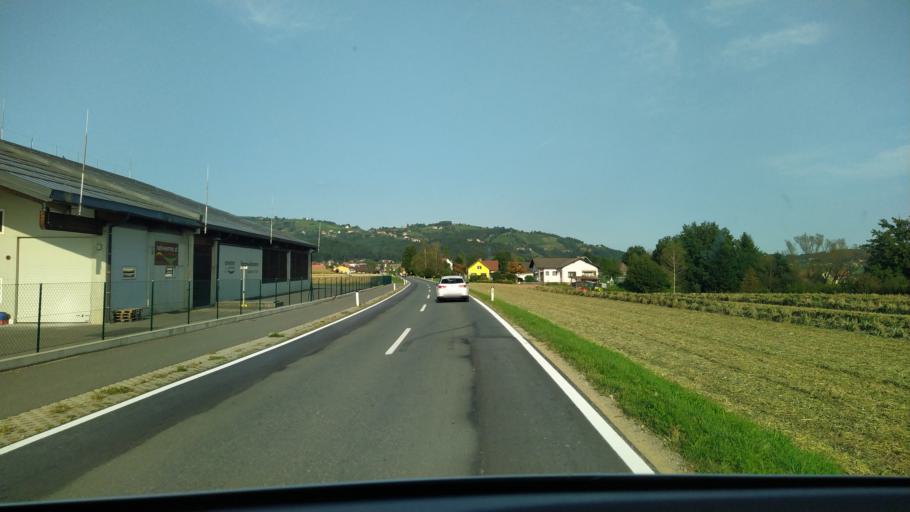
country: AT
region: Styria
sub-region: Politischer Bezirk Leibnitz
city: Gleinstatten
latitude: 46.7571
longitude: 15.3768
